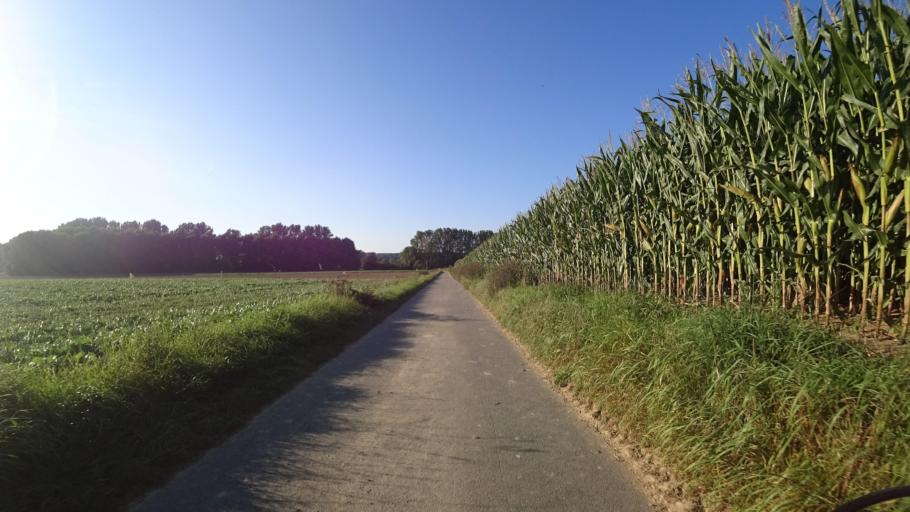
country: BE
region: Wallonia
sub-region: Province du Brabant Wallon
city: Perwez
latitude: 50.5939
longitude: 4.7621
